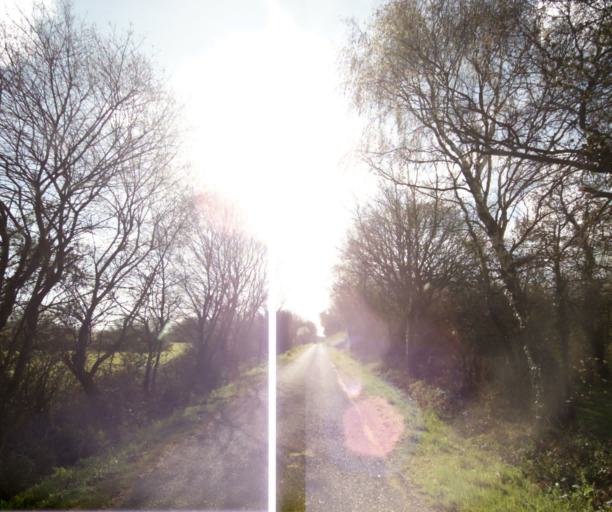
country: FR
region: Pays de la Loire
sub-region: Departement de la Loire-Atlantique
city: Bouvron
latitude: 47.4058
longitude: -1.8367
